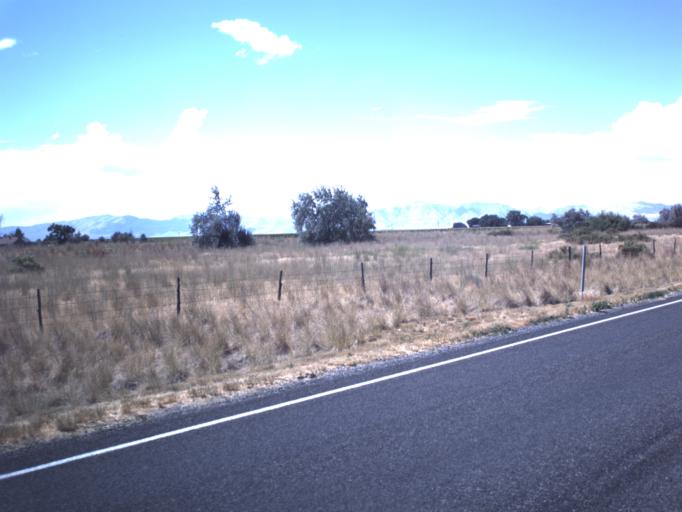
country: US
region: Utah
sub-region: Box Elder County
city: Honeyville
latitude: 41.5669
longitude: -112.1861
